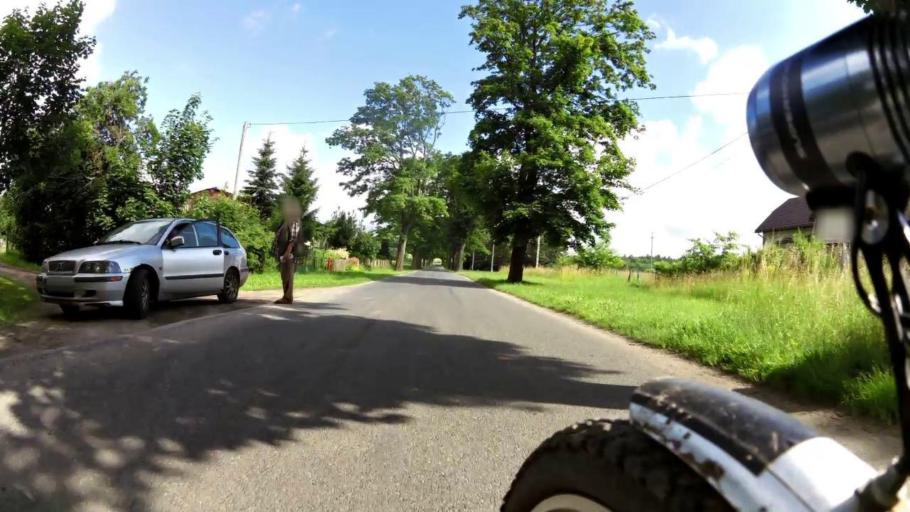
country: PL
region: West Pomeranian Voivodeship
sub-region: Powiat swidwinski
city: Rabino
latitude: 53.7593
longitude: 15.9114
